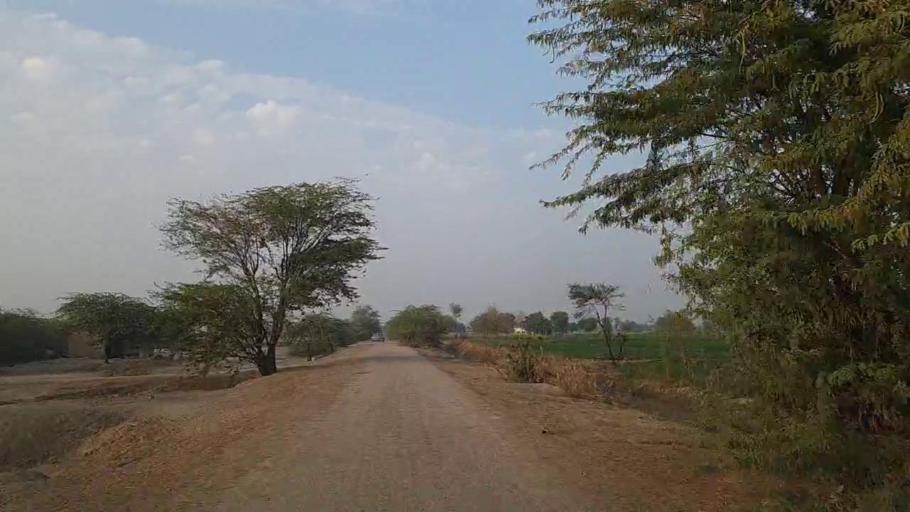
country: PK
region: Sindh
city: Jam Sahib
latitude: 26.3156
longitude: 68.6090
